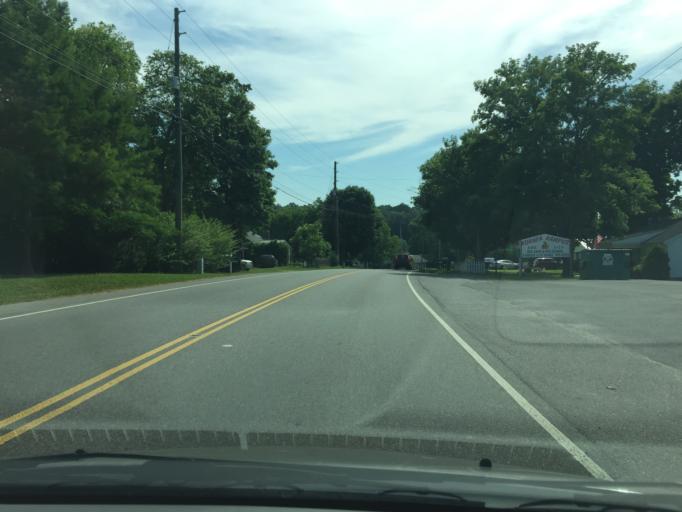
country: US
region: Tennessee
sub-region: Hamilton County
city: Collegedale
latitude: 35.1127
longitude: -84.9848
